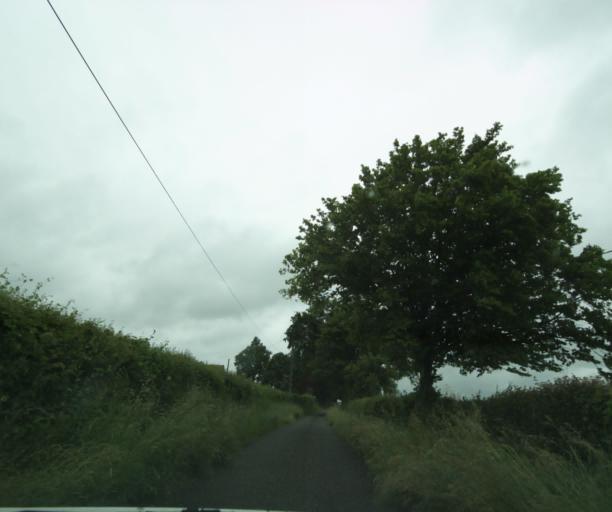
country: FR
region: Bourgogne
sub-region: Departement de Saone-et-Loire
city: Palinges
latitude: 46.5012
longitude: 4.2491
